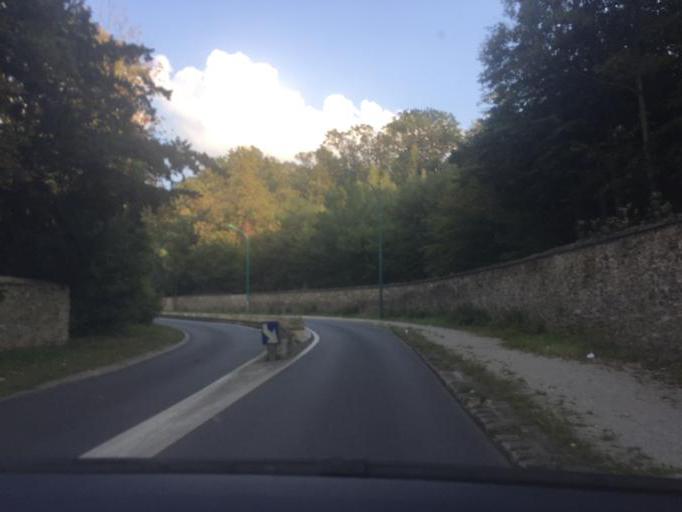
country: FR
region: Ile-de-France
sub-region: Departement des Yvelines
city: Jouy-en-Josas
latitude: 48.7614
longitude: 2.1716
